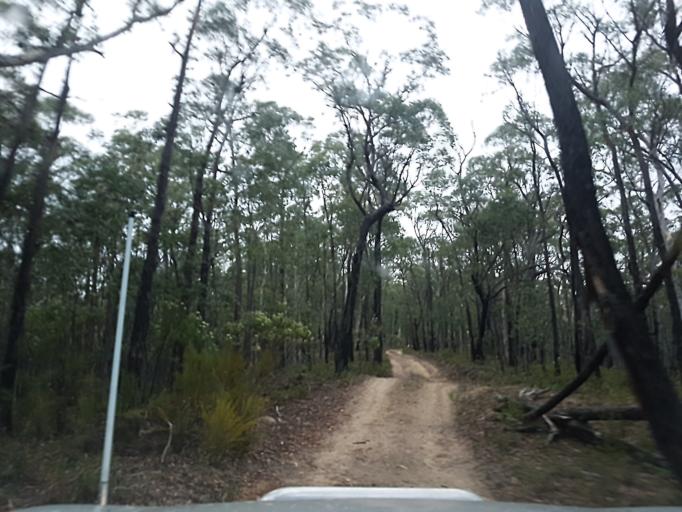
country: AU
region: New South Wales
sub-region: Snowy River
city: Jindabyne
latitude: -36.8520
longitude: 148.2279
